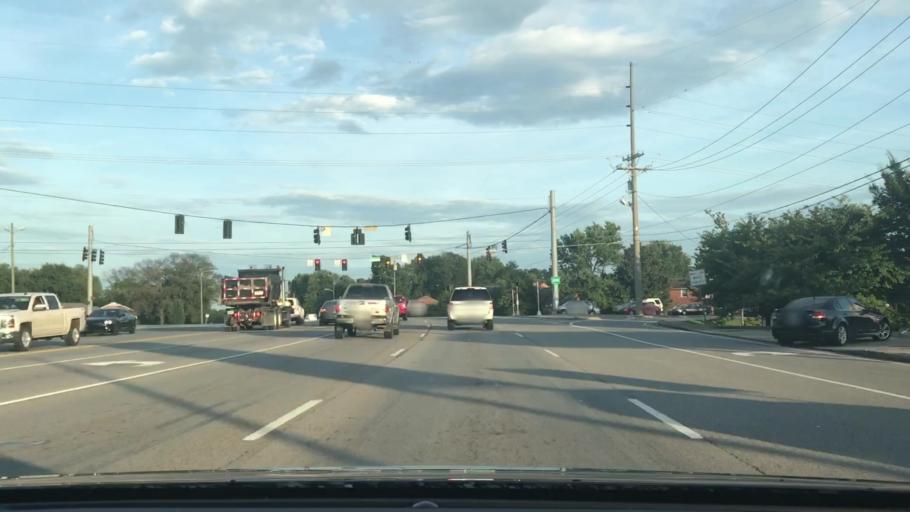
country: US
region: Tennessee
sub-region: Davidson County
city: Oak Hill
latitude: 36.0813
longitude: -86.7593
